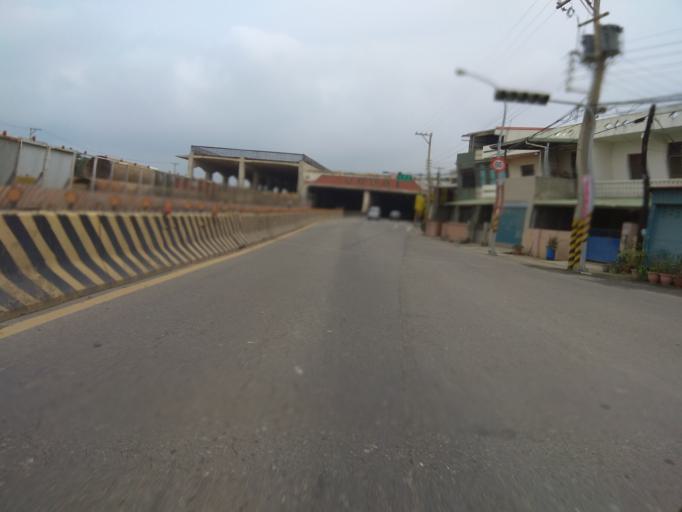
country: TW
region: Taiwan
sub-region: Hsinchu
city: Zhubei
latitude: 24.8769
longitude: 120.9545
